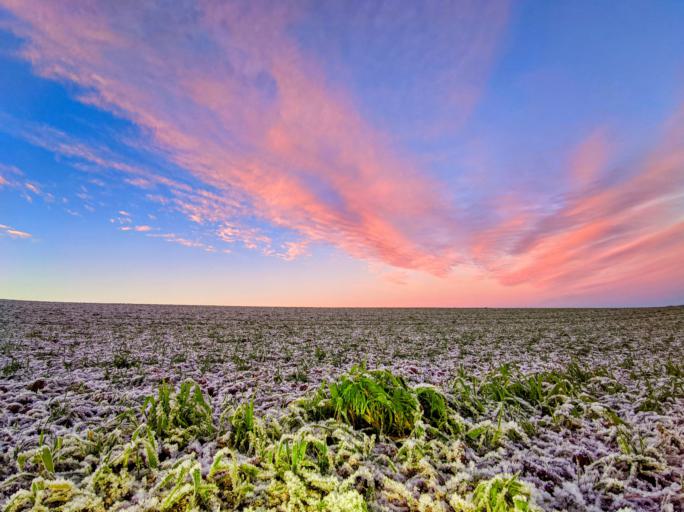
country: NO
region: Akershus
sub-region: Nannestad
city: Teigebyen
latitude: 60.1734
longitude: 11.0127
